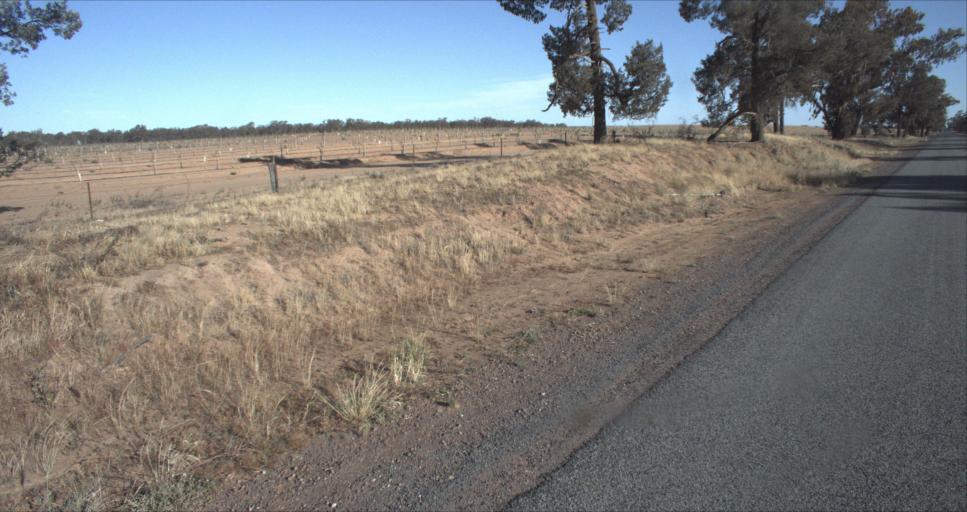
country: AU
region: New South Wales
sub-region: Leeton
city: Leeton
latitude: -34.6445
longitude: 146.3524
